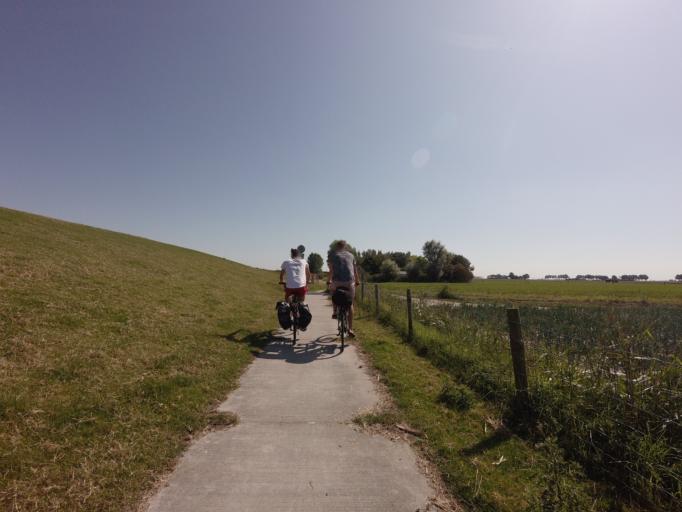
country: NL
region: Friesland
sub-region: Gemeente Dongeradeel
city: Anjum
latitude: 53.3980
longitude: 6.1034
